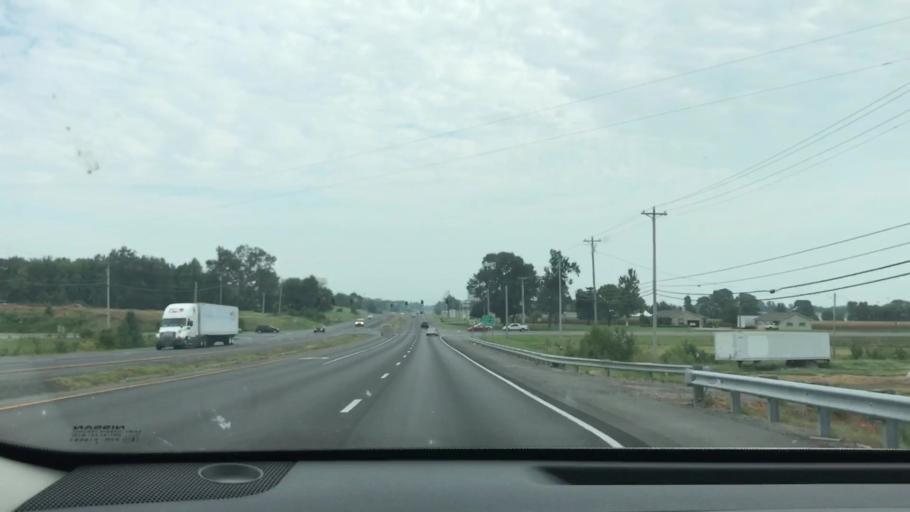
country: US
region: Kentucky
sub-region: Calloway County
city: Murray
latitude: 36.6508
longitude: -88.3070
